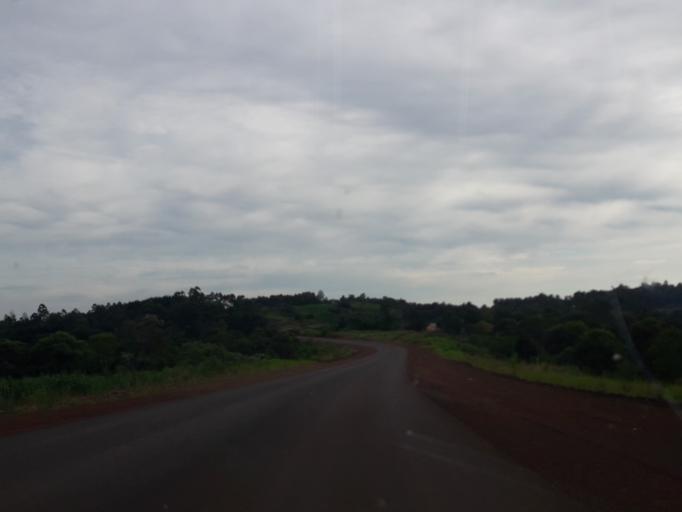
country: AR
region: Misiones
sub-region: Departamento de San Pedro
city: San Pedro
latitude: -26.5185
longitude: -53.9375
